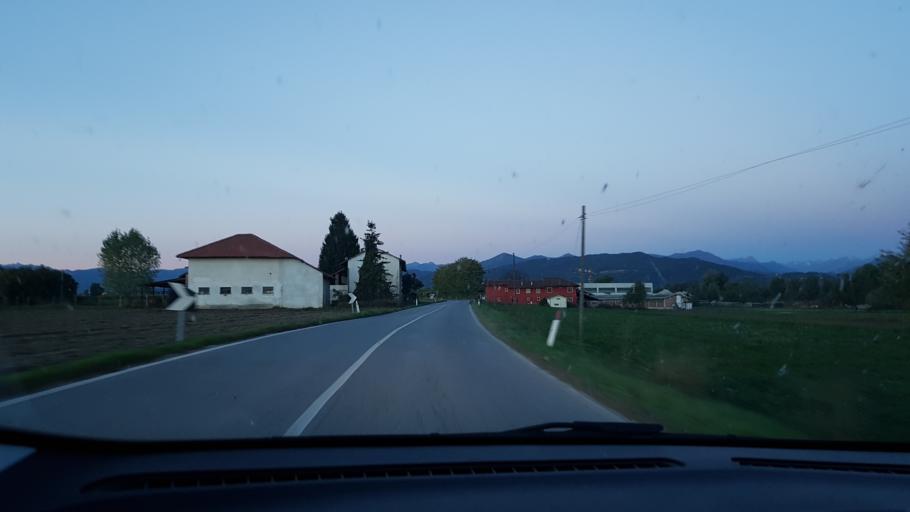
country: IT
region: Piedmont
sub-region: Provincia di Cuneo
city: Villafalletto
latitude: 44.5528
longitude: 7.5538
